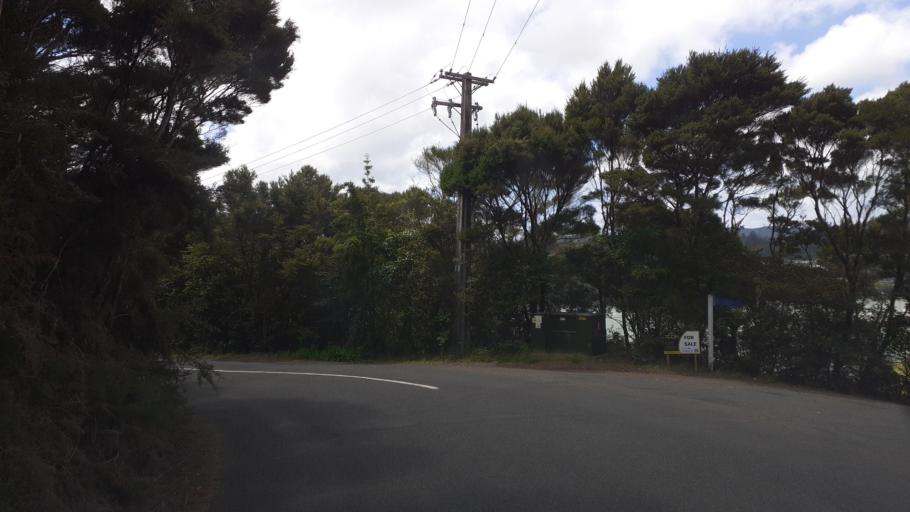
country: NZ
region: Northland
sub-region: Far North District
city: Paihia
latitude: -35.3112
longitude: 174.1141
